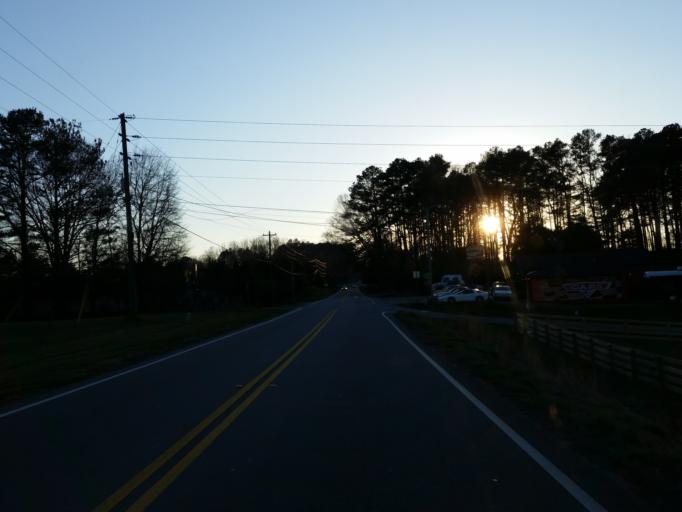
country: US
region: Georgia
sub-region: Cherokee County
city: Holly Springs
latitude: 34.1572
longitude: -84.4302
